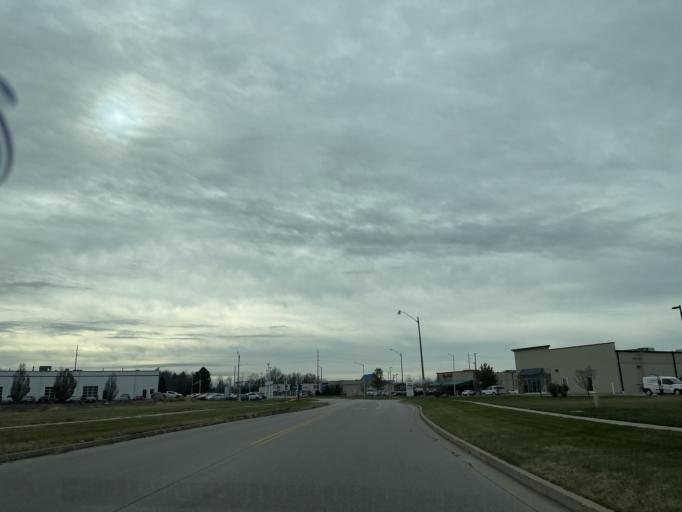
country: US
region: Illinois
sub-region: Sangamon County
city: Jerome
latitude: 39.7587
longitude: -89.7294
